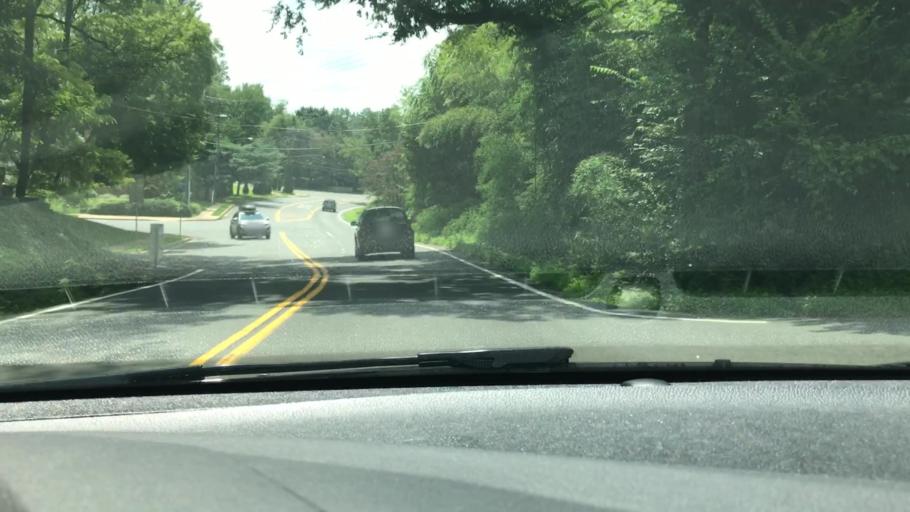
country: US
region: Virginia
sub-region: Fairfax County
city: McLean
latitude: 38.9134
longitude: -77.1657
